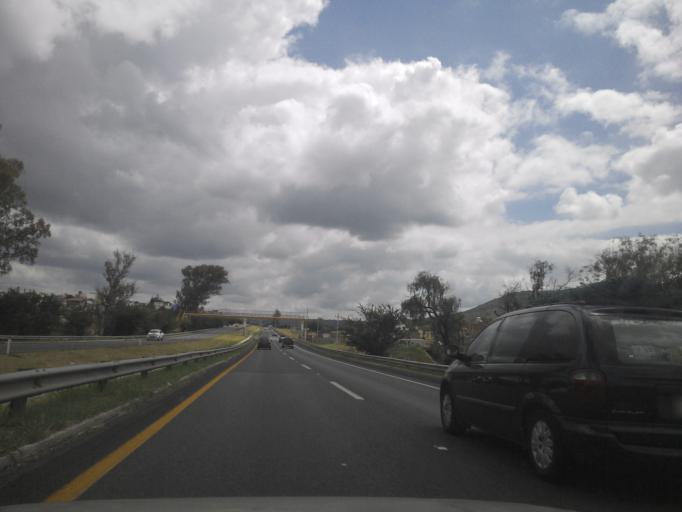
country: MX
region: Jalisco
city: Zapotlanejo
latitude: 20.6172
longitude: -103.0688
